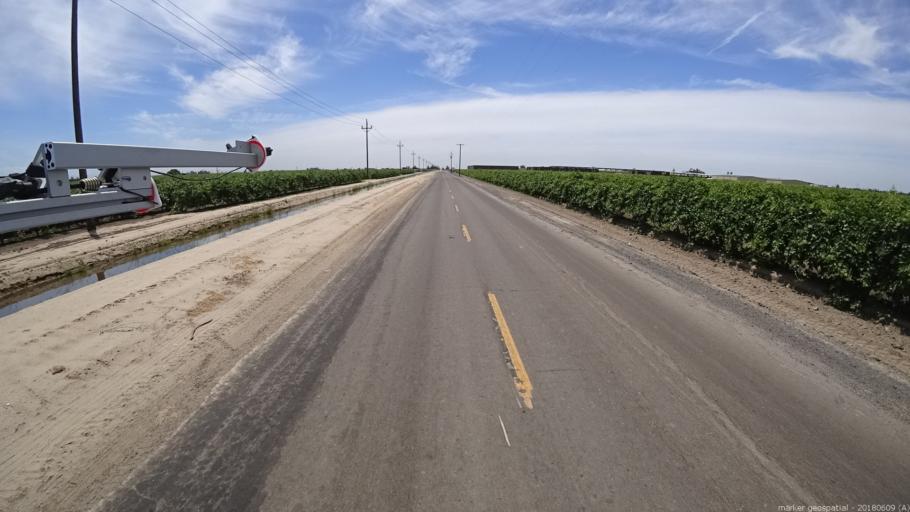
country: US
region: California
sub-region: Madera County
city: Parkwood
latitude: 36.9166
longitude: -120.0393
